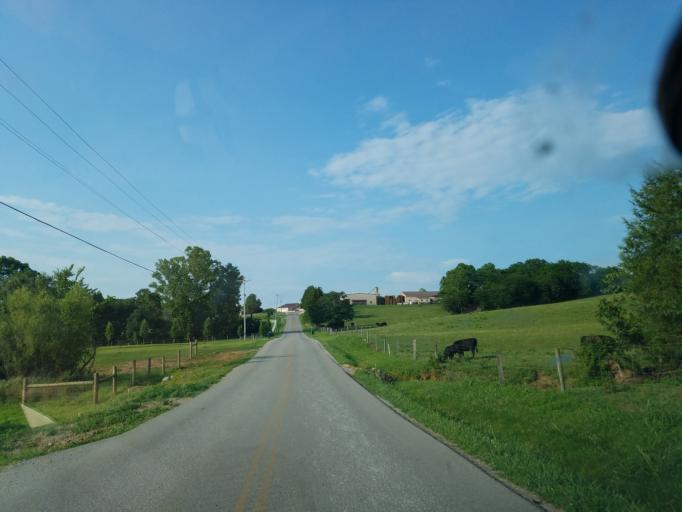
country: US
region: Ohio
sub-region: Adams County
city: West Union
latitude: 38.8948
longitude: -83.5213
